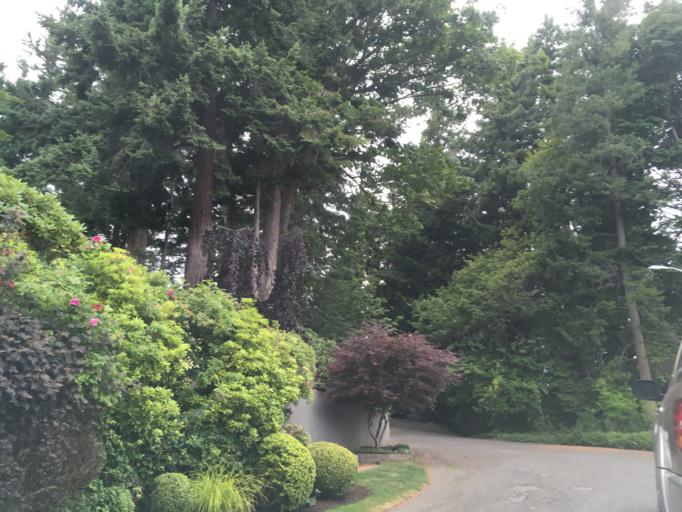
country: US
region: Washington
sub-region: Whatcom County
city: Bellingham
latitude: 48.7120
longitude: -122.5058
